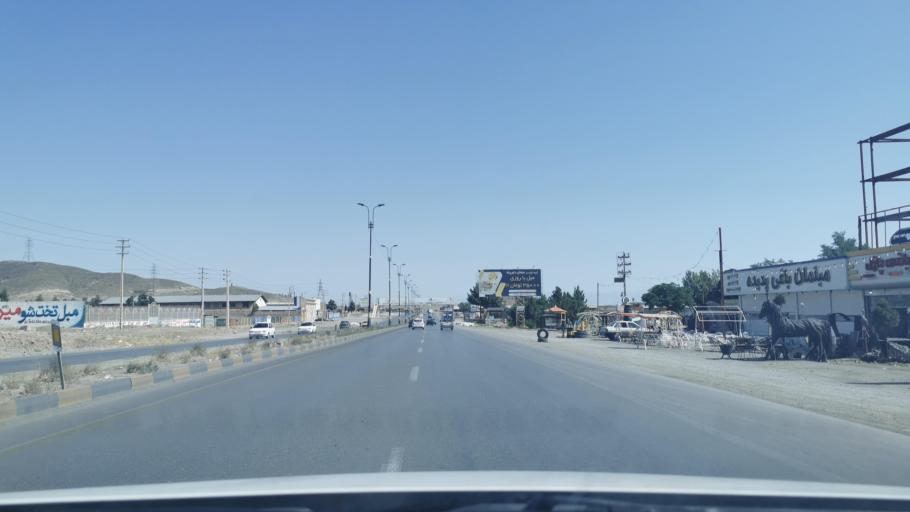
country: IR
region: Razavi Khorasan
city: Torqabeh
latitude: 36.3783
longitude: 59.4156
